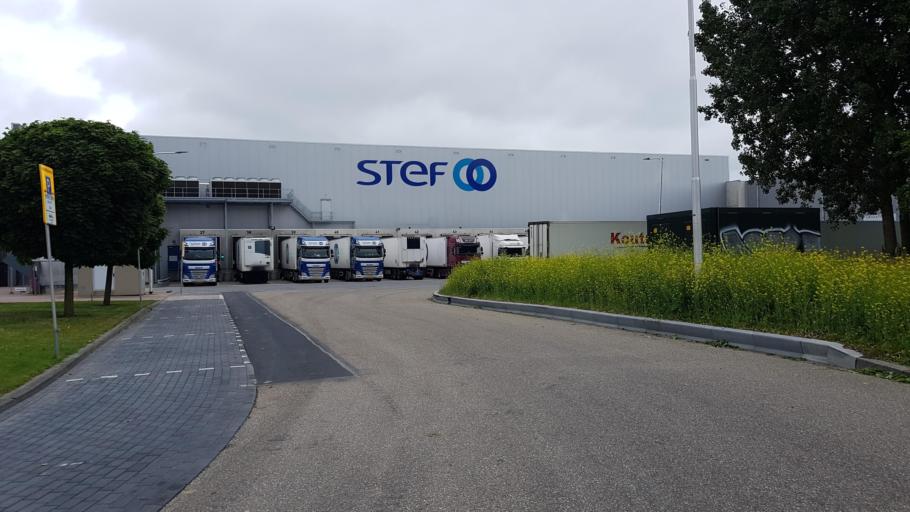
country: NL
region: South Holland
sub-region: Bodegraven-Reeuwijk
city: Bodegraven
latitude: 52.0678
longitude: 4.7580
